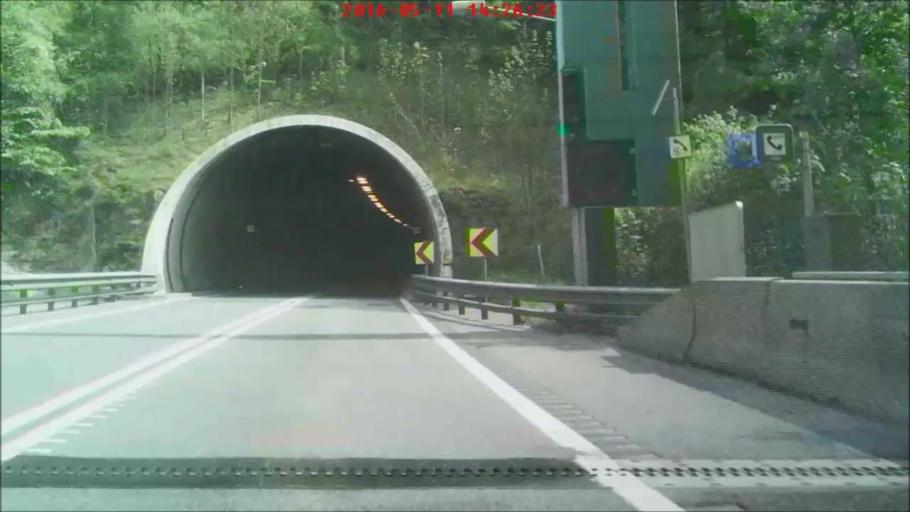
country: AT
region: Upper Austria
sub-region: Politischer Bezirk Kirchdorf an der Krems
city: Micheldorf in Oberoesterreich
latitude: 47.8178
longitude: 14.1694
